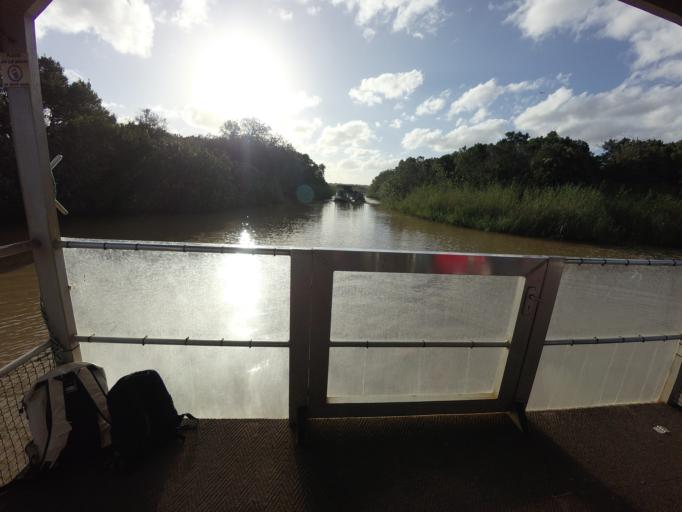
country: ZA
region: KwaZulu-Natal
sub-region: uMkhanyakude District Municipality
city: Mtubatuba
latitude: -28.3623
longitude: 32.4102
